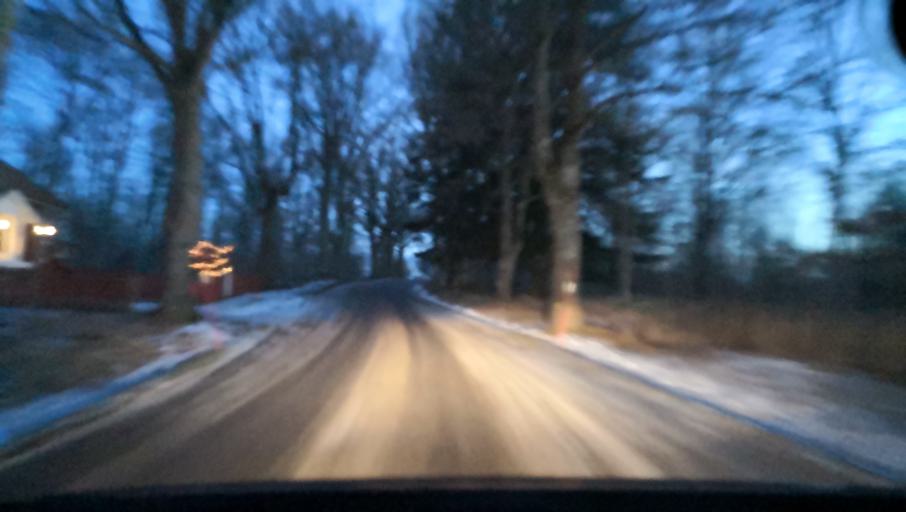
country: SE
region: Soedermanland
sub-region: Katrineholms Kommun
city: Katrineholm
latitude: 59.0725
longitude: 16.3353
